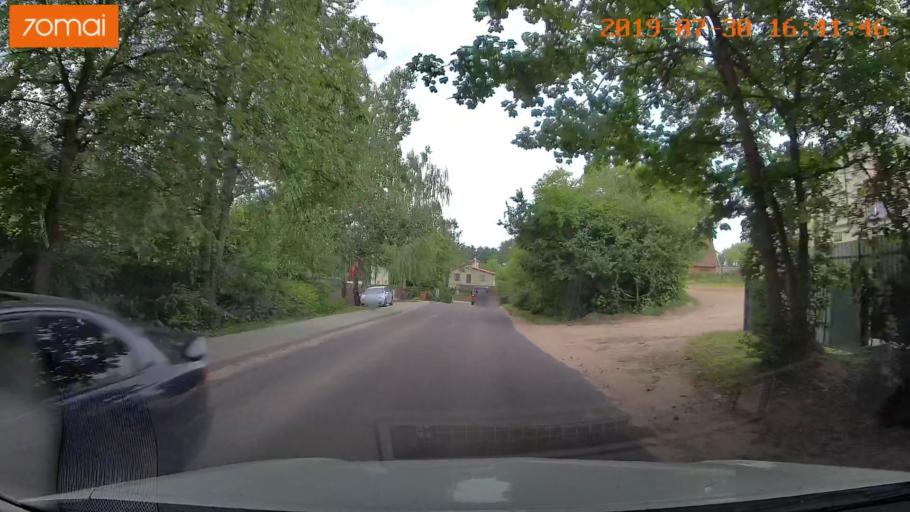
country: LT
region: Vilnius County
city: Rasos
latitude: 54.7136
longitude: 25.3521
